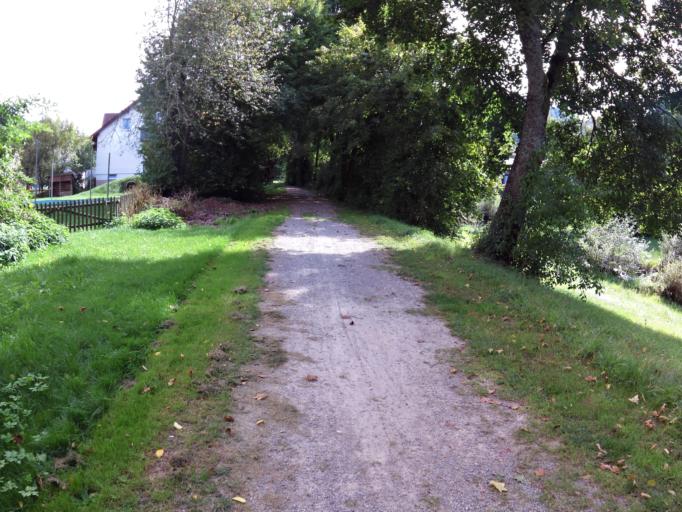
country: DE
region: Baden-Wuerttemberg
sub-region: Freiburg Region
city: Oberndorf
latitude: 48.3121
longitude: 8.5716
